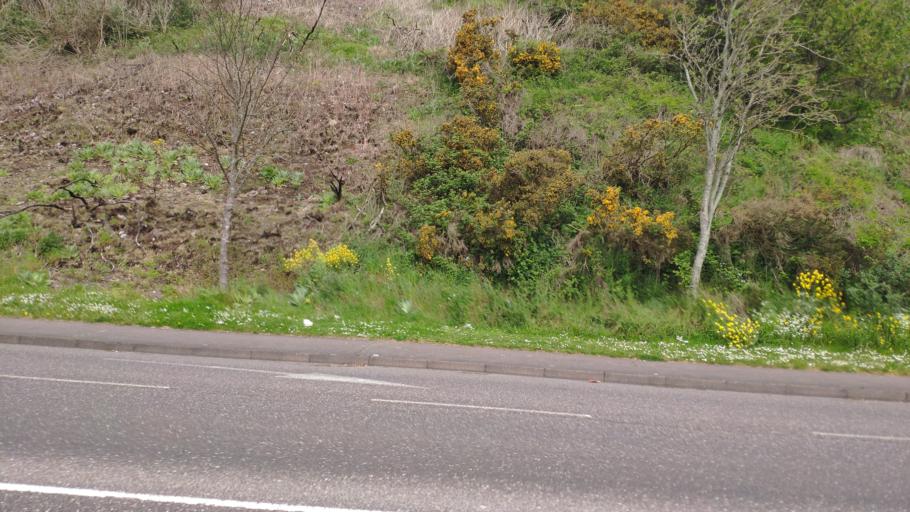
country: IE
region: Munster
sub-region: County Cork
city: Cork
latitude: 51.9149
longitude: -8.4584
